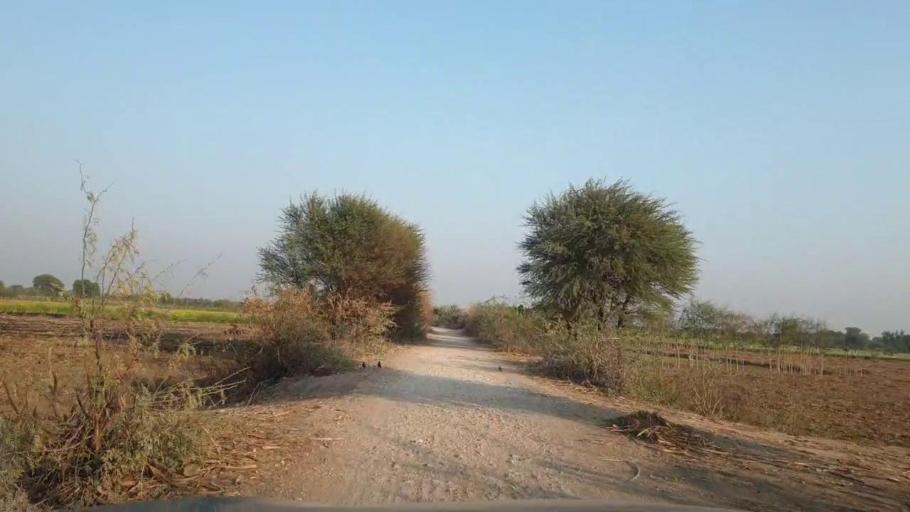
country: PK
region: Sindh
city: Tando Allahyar
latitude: 25.5549
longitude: 68.8525
